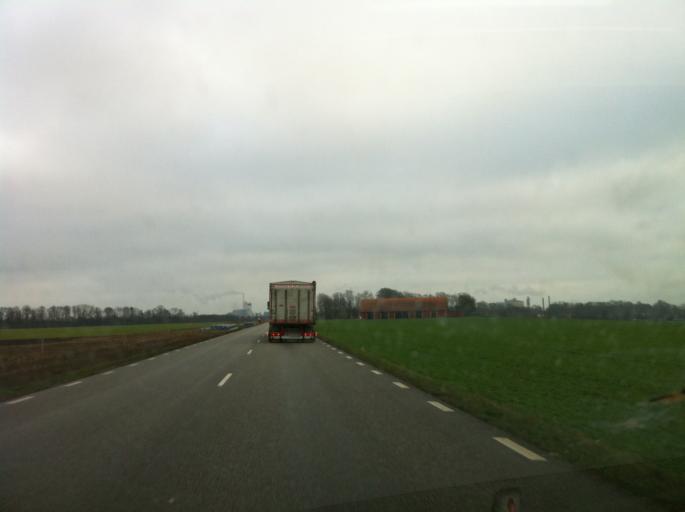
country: SE
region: Skane
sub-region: Eslovs Kommun
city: Eslov
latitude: 55.7905
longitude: 13.2273
